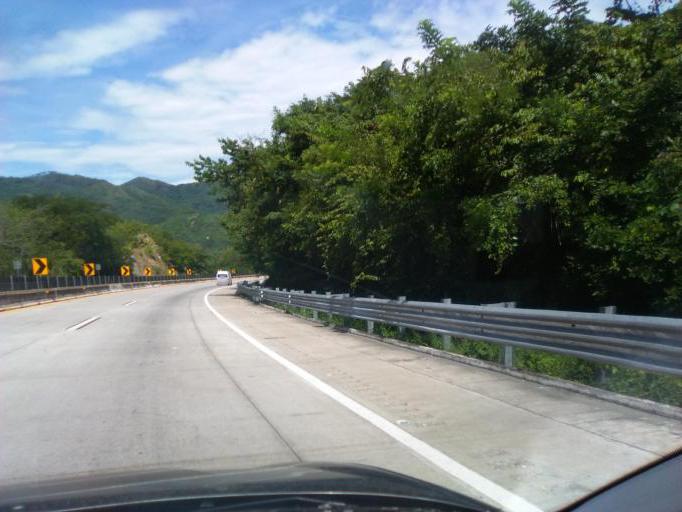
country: MX
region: Guerrero
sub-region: Acapulco de Juarez
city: Pueblo Madero (El Playon)
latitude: 17.0889
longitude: -99.5980
